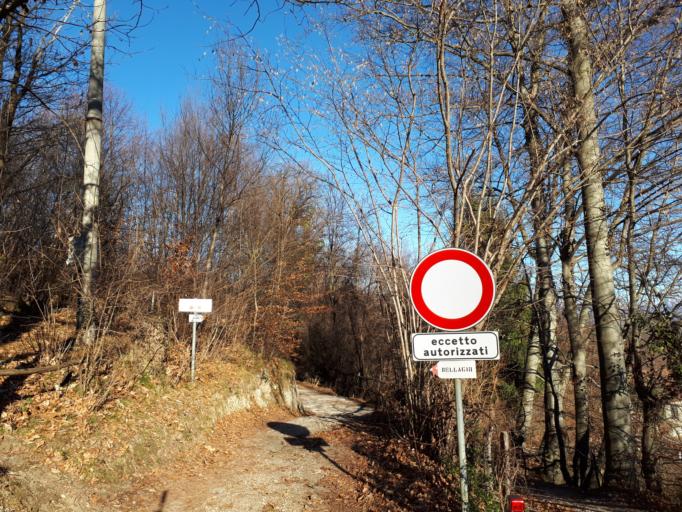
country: IT
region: Lombardy
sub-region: Provincia di Como
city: Cadenabbia
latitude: 45.9609
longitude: 9.2464
